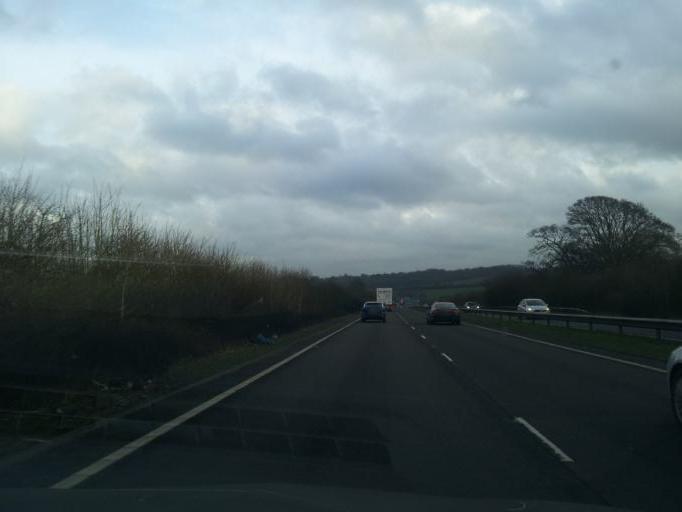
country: GB
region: England
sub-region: Hertfordshire
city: Bovingdon
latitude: 51.7459
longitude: -0.5444
